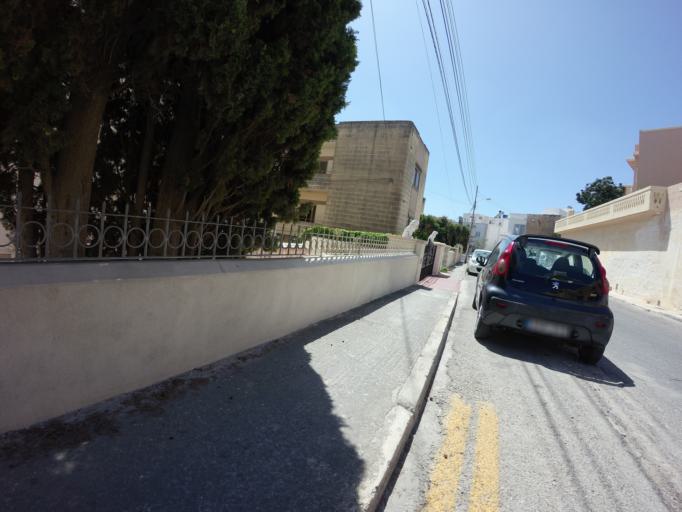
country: MT
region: Il-Gzira
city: Gzira
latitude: 35.9066
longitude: 14.4874
